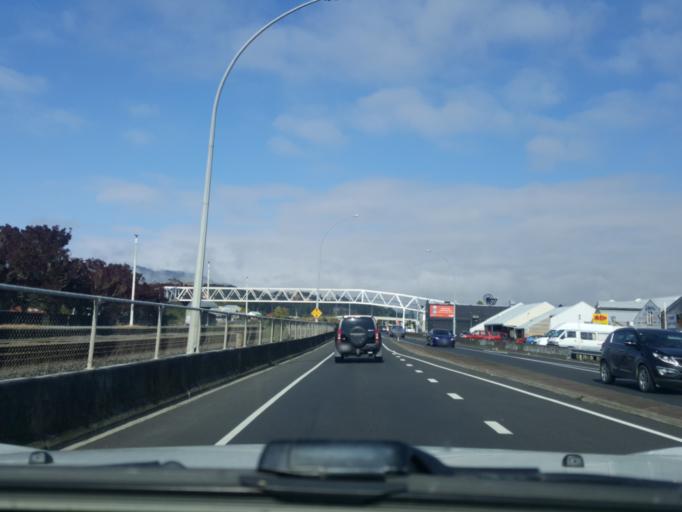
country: NZ
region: Waikato
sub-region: Waikato District
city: Ngaruawahia
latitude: -37.5570
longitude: 175.1595
